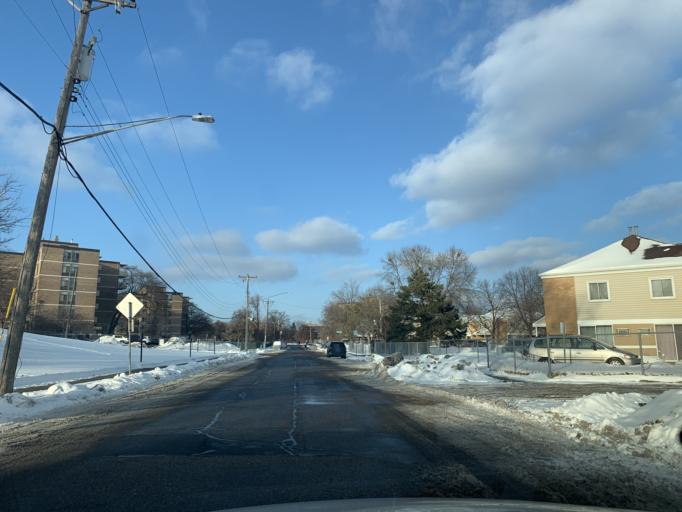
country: US
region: Minnesota
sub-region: Hennepin County
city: Minneapolis
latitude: 44.9819
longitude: -93.2982
